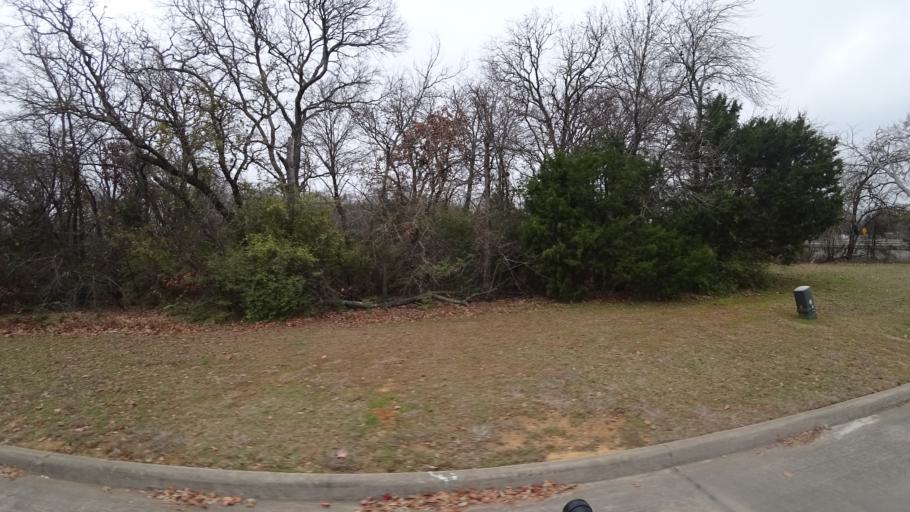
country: US
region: Texas
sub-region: Denton County
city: Lewisville
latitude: 33.0280
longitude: -97.0358
